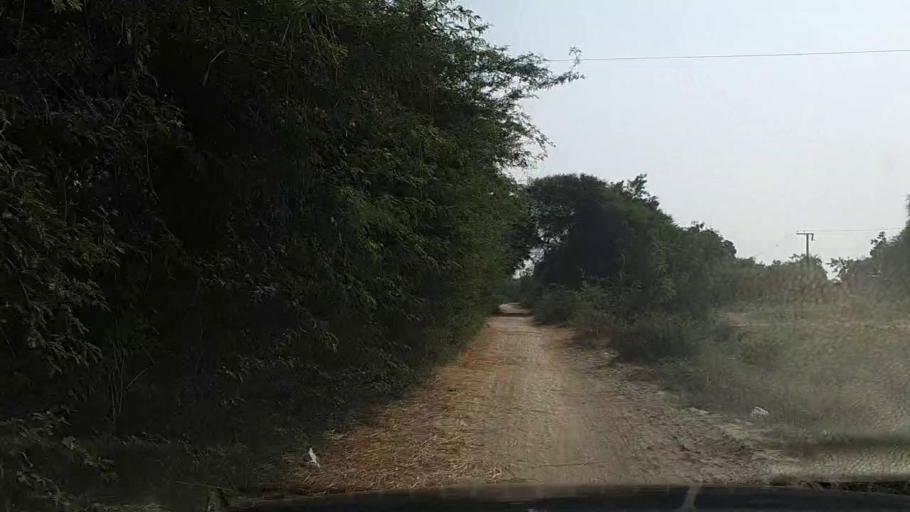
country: PK
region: Sindh
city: Mirpur Batoro
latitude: 24.7020
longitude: 68.2177
